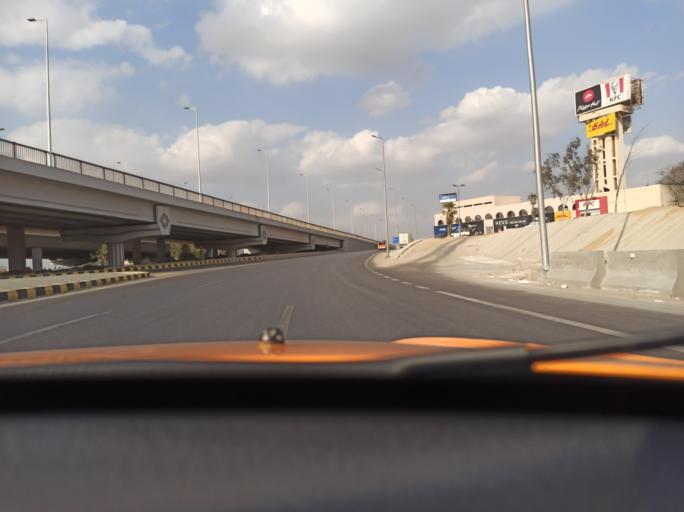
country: EG
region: Eastern Province
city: Bilbays
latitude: 30.2411
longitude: 31.7214
